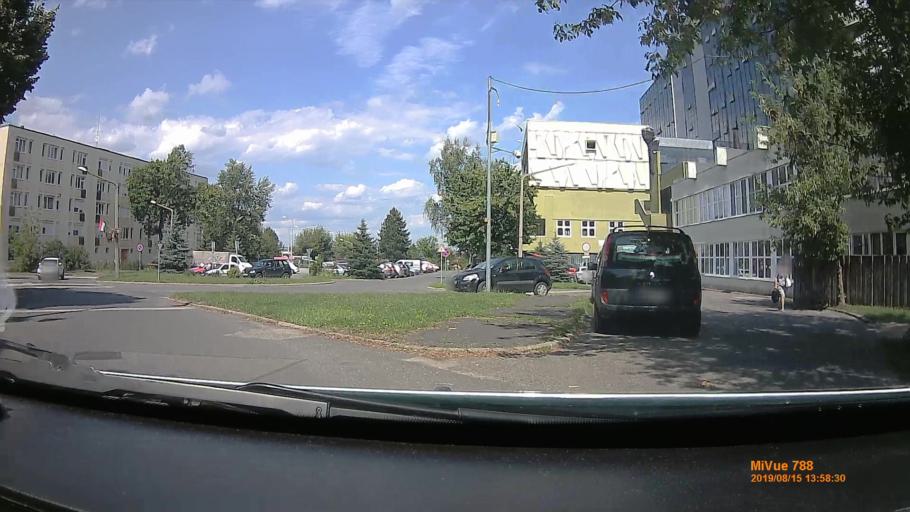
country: HU
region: Borsod-Abauj-Zemplen
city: Kazincbarcika
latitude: 48.2542
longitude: 20.6182
